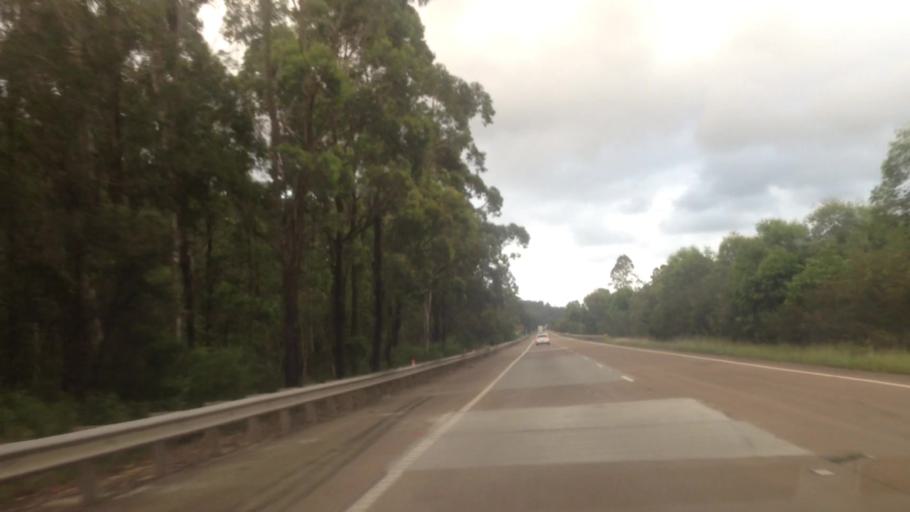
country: AU
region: New South Wales
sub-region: Wyong Shire
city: Charmhaven
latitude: -33.1678
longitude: 151.4676
